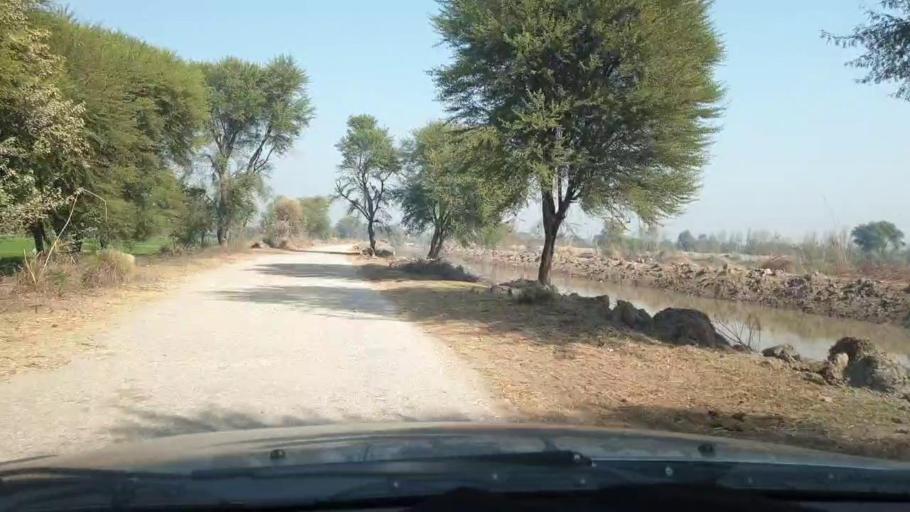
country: PK
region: Sindh
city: Khanpur
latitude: 27.7739
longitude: 69.5362
